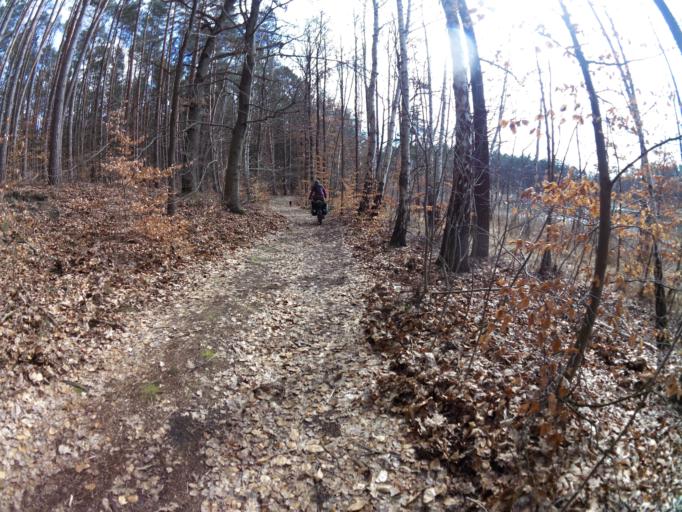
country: PL
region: West Pomeranian Voivodeship
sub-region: Powiat mysliborski
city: Mysliborz
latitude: 52.8454
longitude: 14.8384
